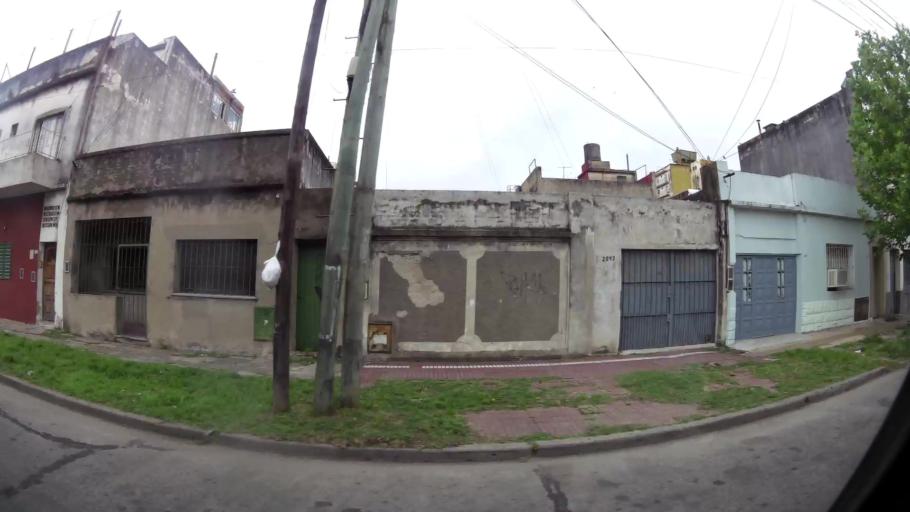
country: AR
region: Buenos Aires
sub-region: Partido de Avellaneda
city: Avellaneda
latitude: -34.6690
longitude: -58.3519
